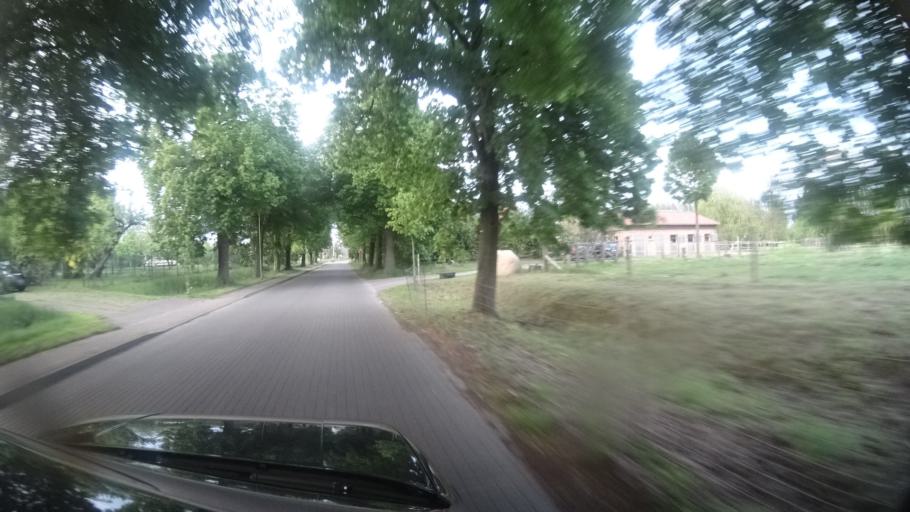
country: DE
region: Brandenburg
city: Ruthnick
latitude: 52.8247
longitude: 12.9659
